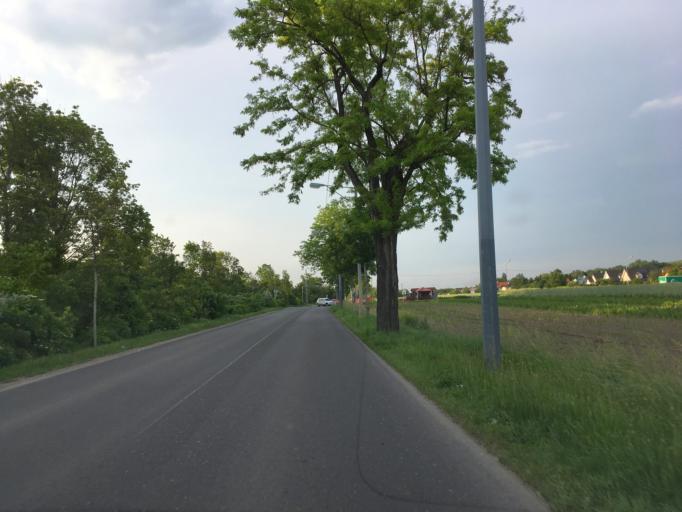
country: AT
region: Lower Austria
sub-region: Politischer Bezirk Wien-Umgebung
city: Gerasdorf bei Wien
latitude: 48.2731
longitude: 16.4572
